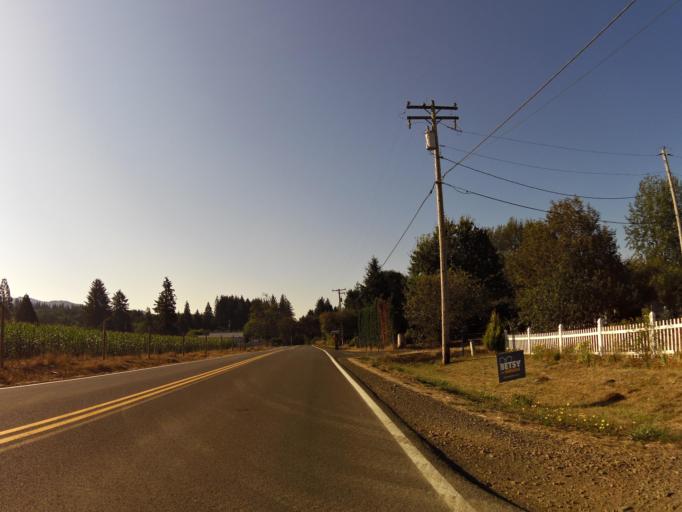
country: US
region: Oregon
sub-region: Tillamook County
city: Tillamook
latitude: 45.3887
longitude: -123.7946
